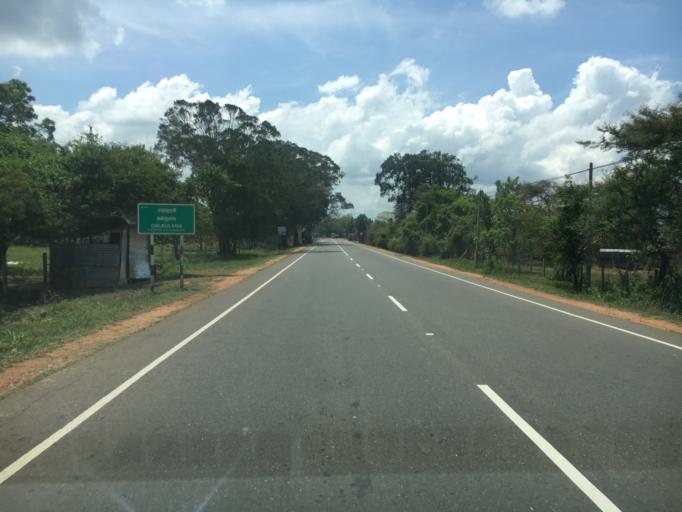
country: LK
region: North Central
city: Anuradhapura
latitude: 8.2763
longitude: 80.4984
